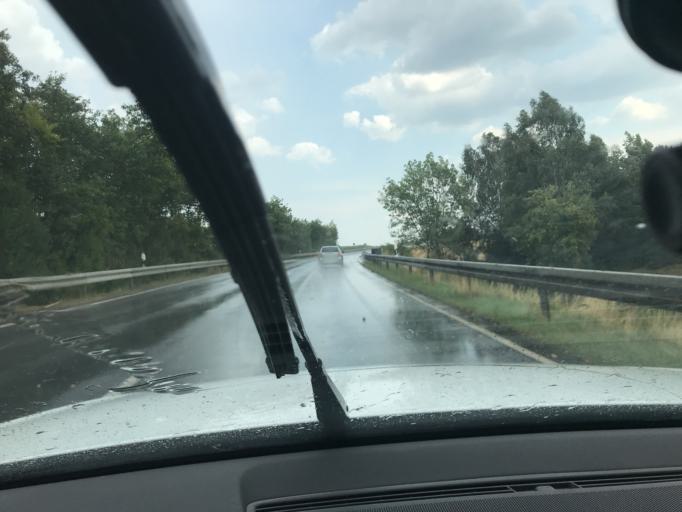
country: DE
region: Bavaria
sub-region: Upper Palatinate
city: Speinshart
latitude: 49.7477
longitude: 11.8527
